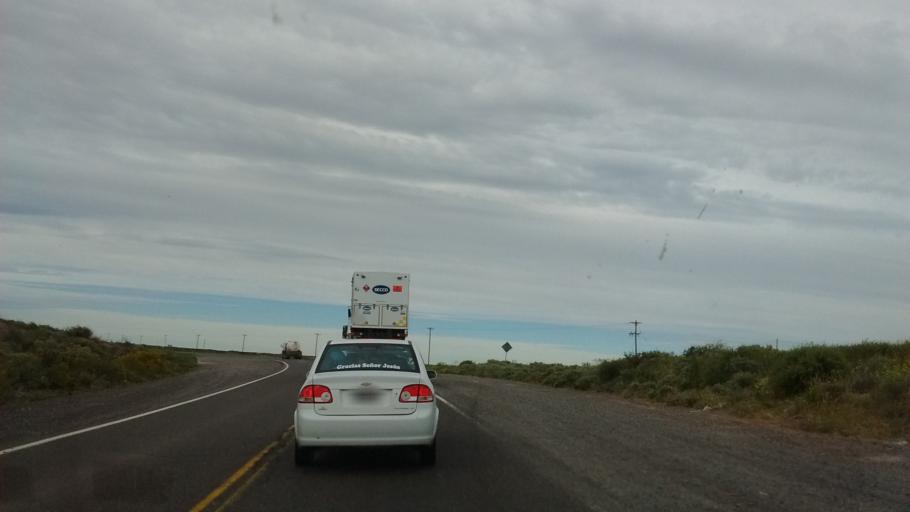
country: AR
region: Rio Negro
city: Catriel
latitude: -38.2064
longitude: -67.9749
